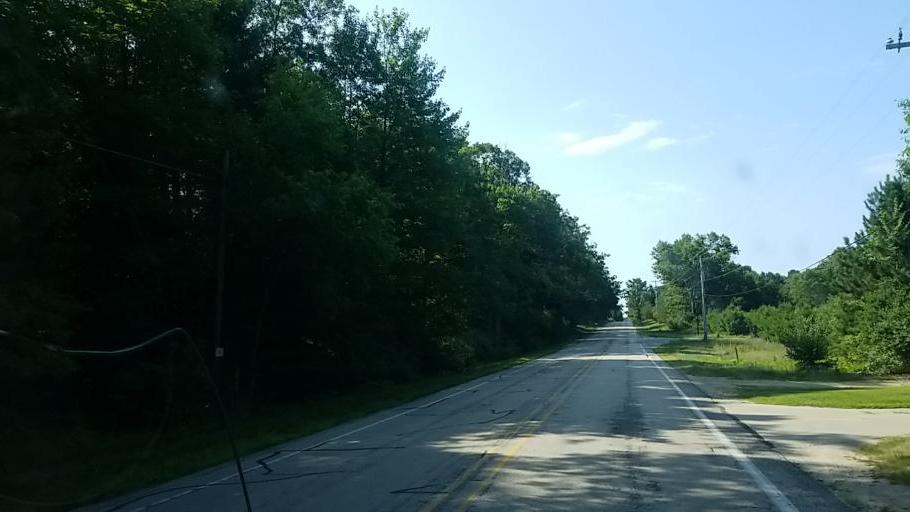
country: US
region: Michigan
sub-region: Muskegon County
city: Whitehall
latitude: 43.3313
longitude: -86.3768
